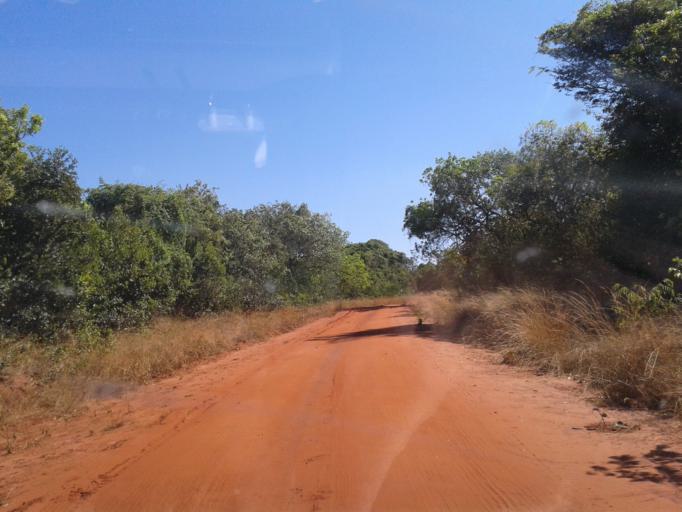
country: BR
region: Minas Gerais
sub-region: Monte Alegre De Minas
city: Monte Alegre de Minas
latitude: -18.8672
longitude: -49.1339
